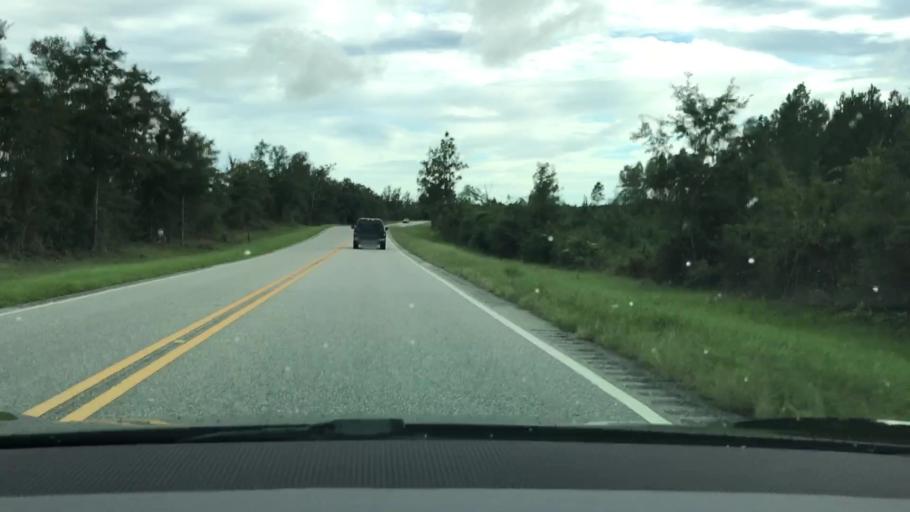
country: US
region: Alabama
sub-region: Geneva County
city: Samson
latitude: 31.0089
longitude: -86.1277
